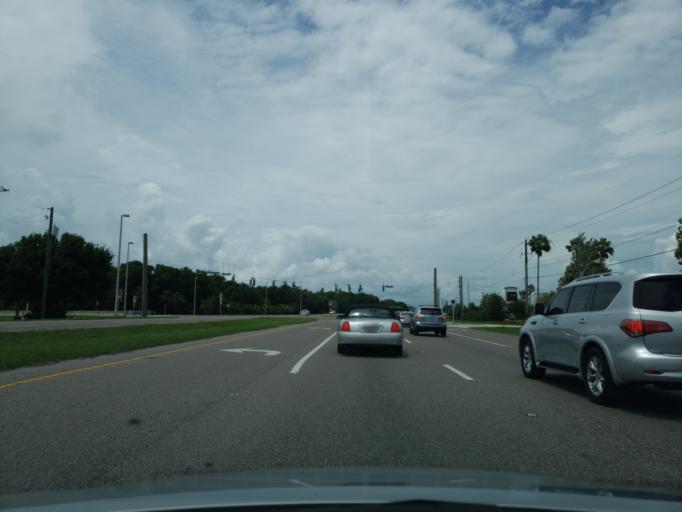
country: US
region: Florida
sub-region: Hillsborough County
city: Carrollwood Village
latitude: 28.0345
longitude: -82.5413
